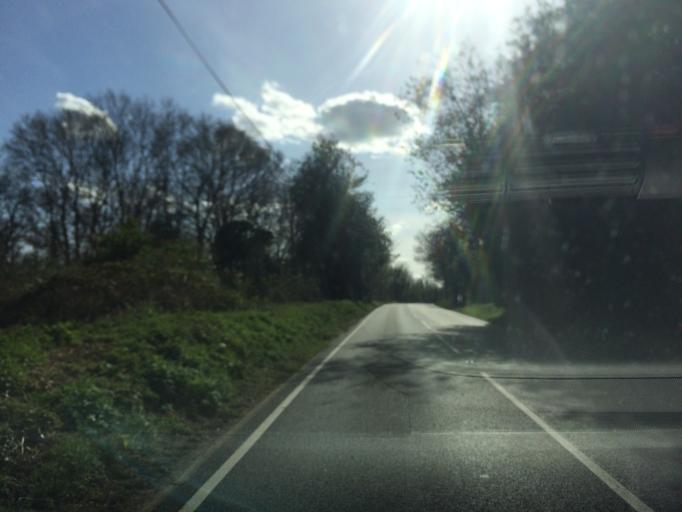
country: GB
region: England
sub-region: Surrey
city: Ottershaw
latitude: 51.3571
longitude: -0.5528
